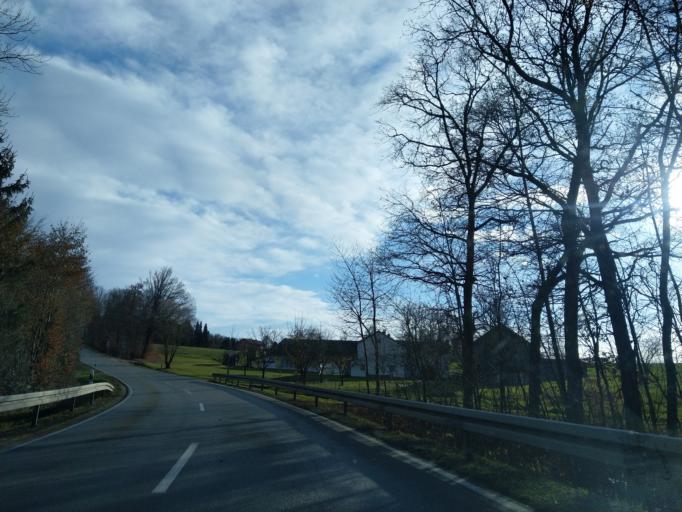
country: DE
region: Bavaria
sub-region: Lower Bavaria
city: Aldersbach
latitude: 48.6302
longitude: 13.0541
